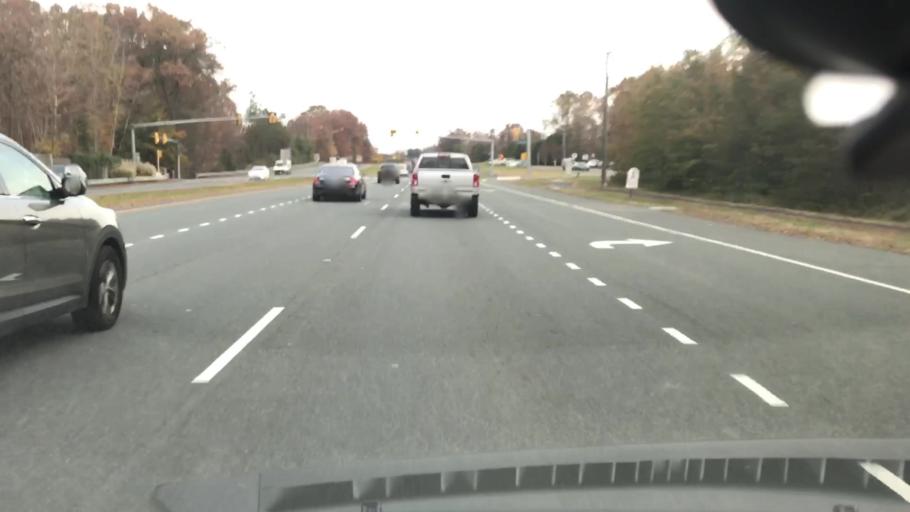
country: US
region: Virginia
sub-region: Fairfax County
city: Fairfax Station
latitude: 38.7943
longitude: -77.3258
